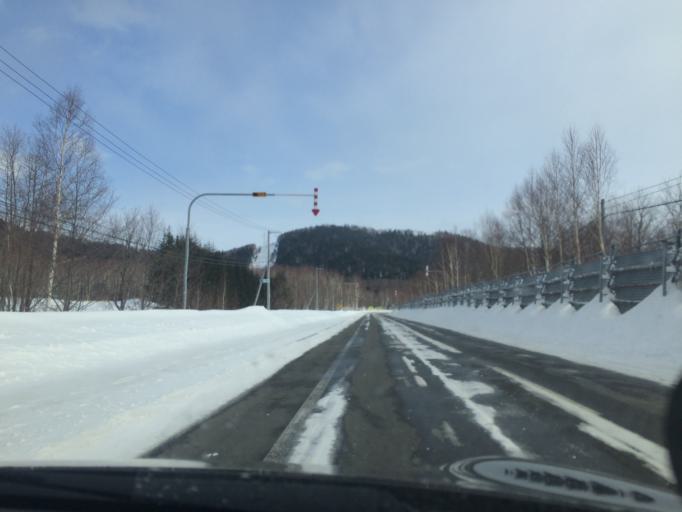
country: JP
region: Hokkaido
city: Shimo-furano
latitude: 43.0542
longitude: 142.6388
